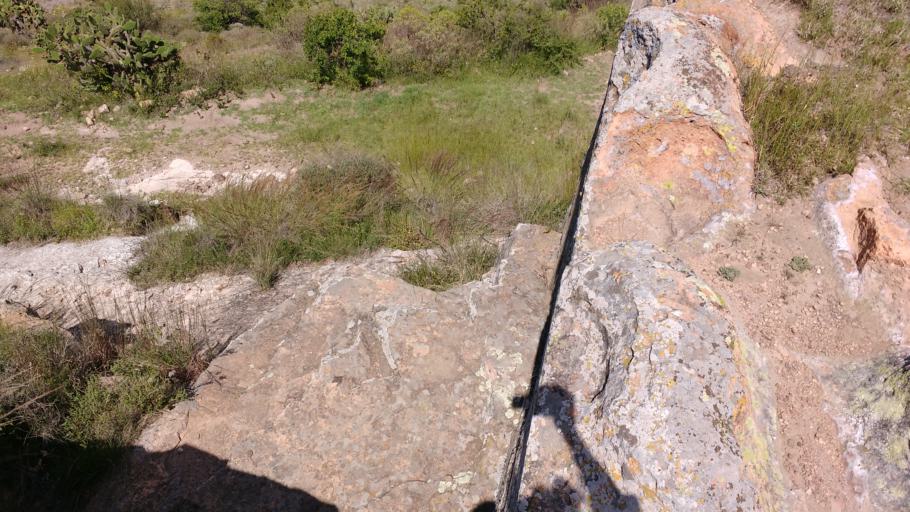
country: MX
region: Hidalgo
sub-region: Tezontepec de Aldama
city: Tenango
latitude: 20.2356
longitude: -99.2760
